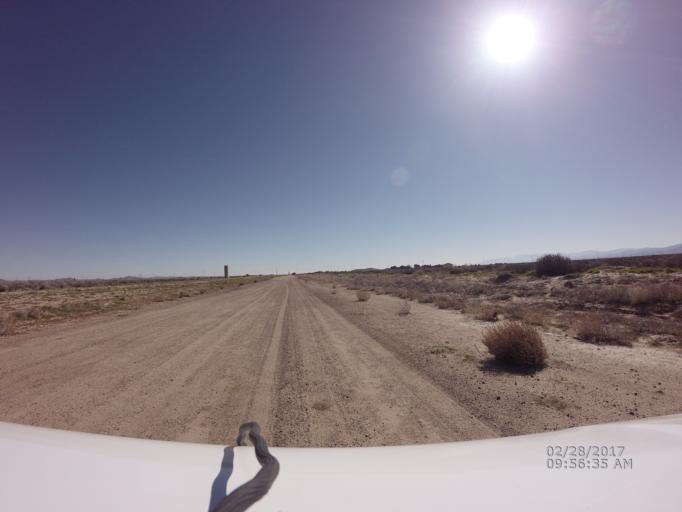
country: US
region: California
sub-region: Kern County
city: Rosamond
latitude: 34.8050
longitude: -118.3355
